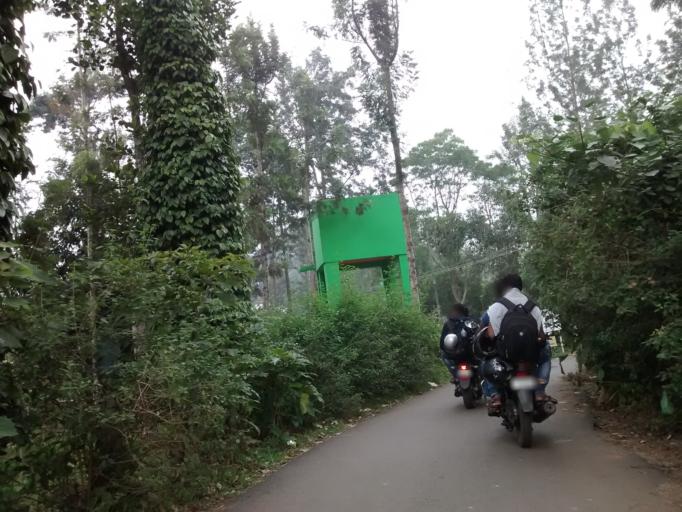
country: IN
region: Tamil Nadu
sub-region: Salem
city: Salem
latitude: 11.7866
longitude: 78.2073
